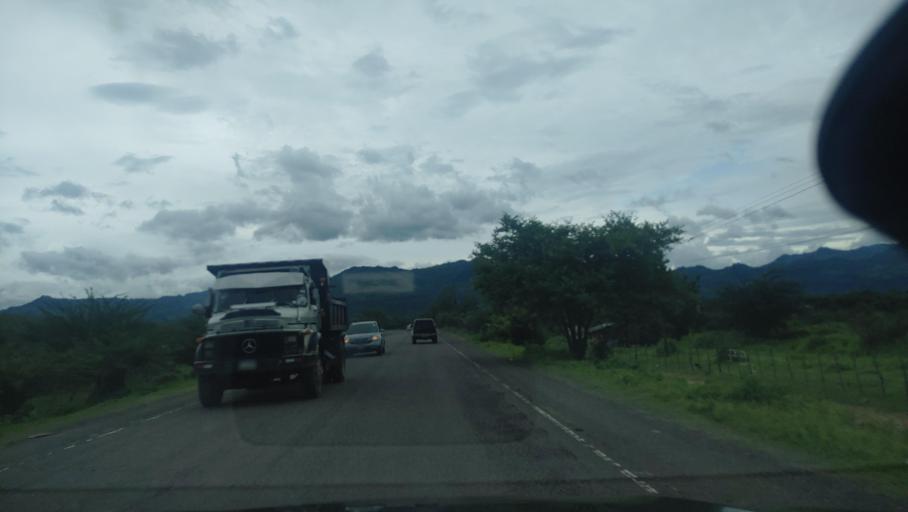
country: HN
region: Choluteca
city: Santa Ana de Yusguare
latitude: 13.3498
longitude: -87.1113
